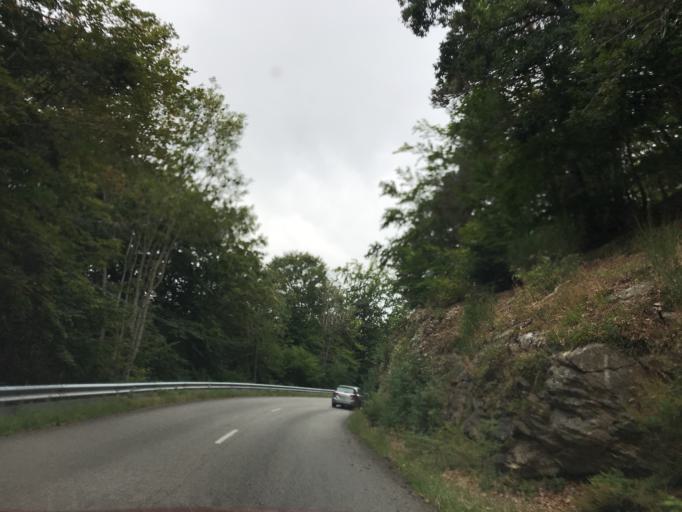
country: FR
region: Rhone-Alpes
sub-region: Departement de la Loire
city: Sail-sous-Couzan
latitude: 45.6946
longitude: 3.8850
